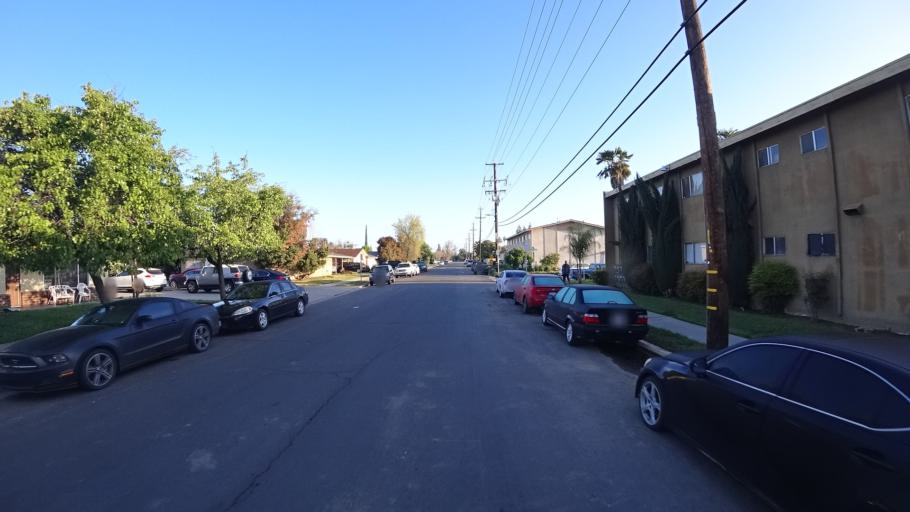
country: US
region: California
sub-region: Fresno County
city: Clovis
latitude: 36.8128
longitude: -119.7655
